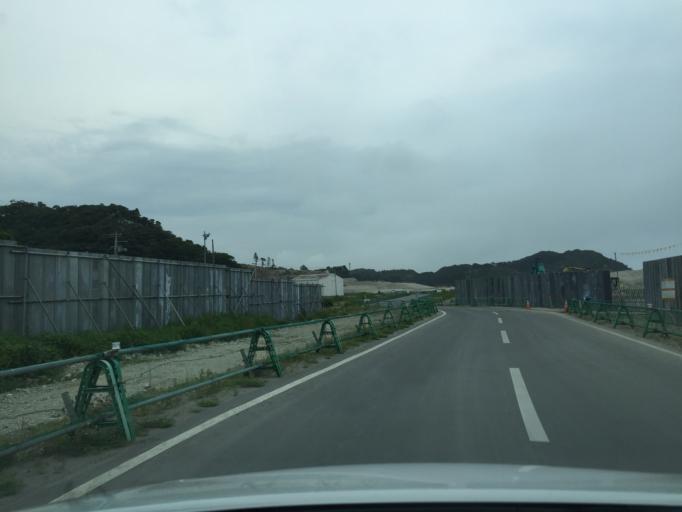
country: JP
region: Fukushima
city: Iwaki
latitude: 37.0001
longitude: 140.9780
